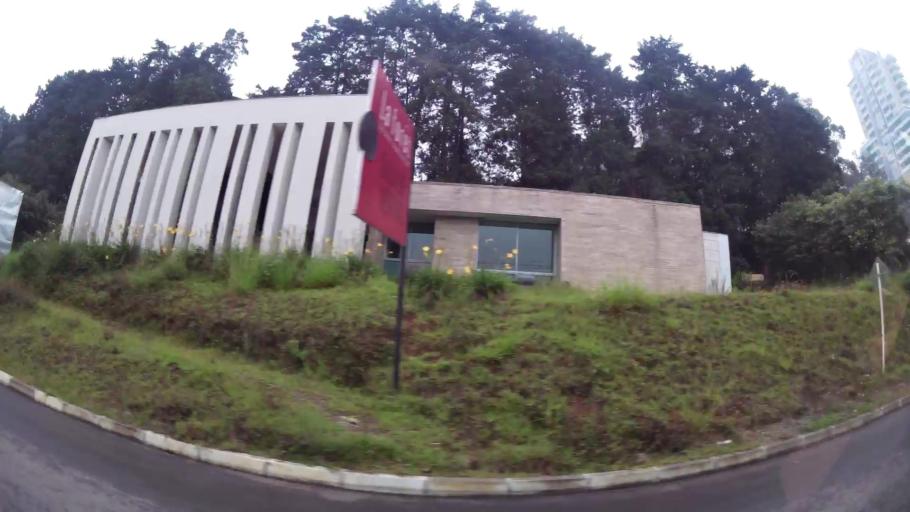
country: CO
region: Antioquia
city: Envigado
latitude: 6.1857
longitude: -75.5589
